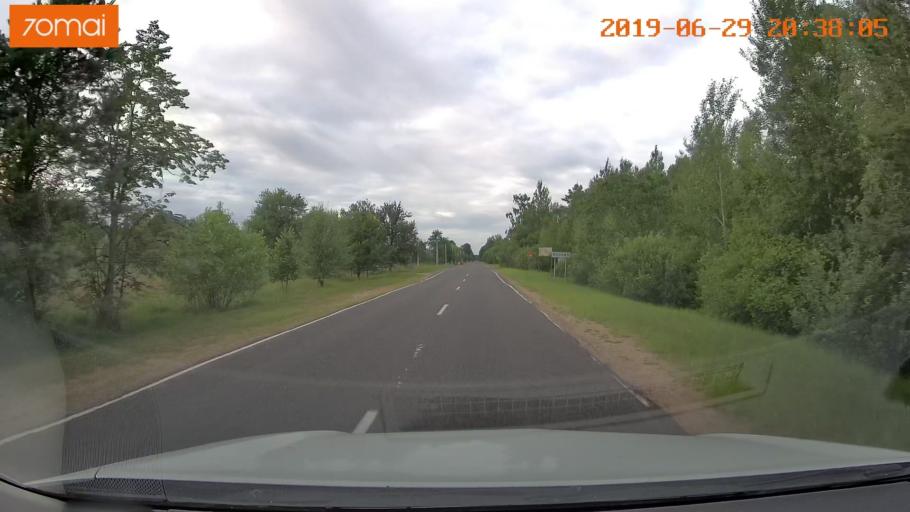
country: BY
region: Brest
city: Hantsavichy
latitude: 52.5459
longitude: 26.3652
